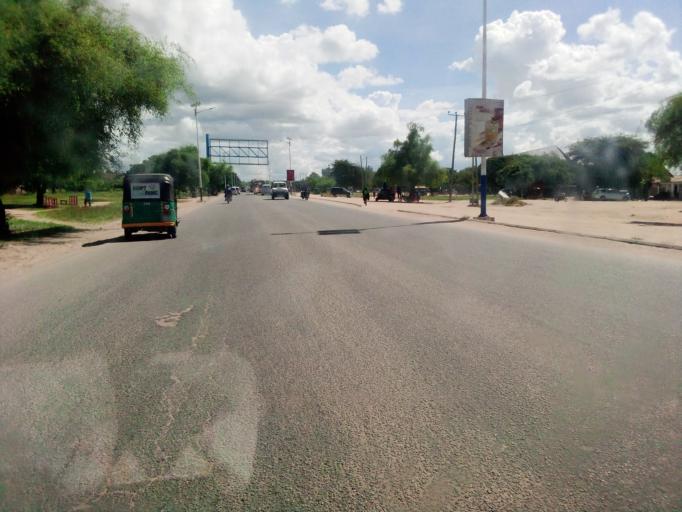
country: TZ
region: Dodoma
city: Dodoma
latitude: -6.1760
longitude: 35.7615
